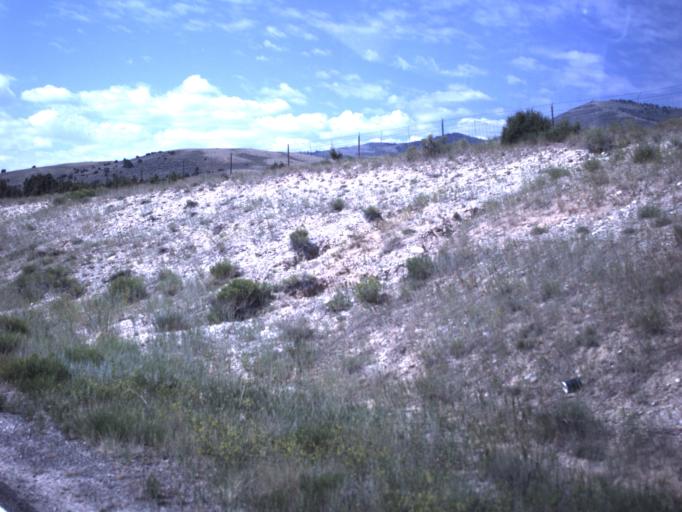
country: US
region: Utah
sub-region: Daggett County
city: Manila
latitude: 40.9931
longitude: -109.8442
